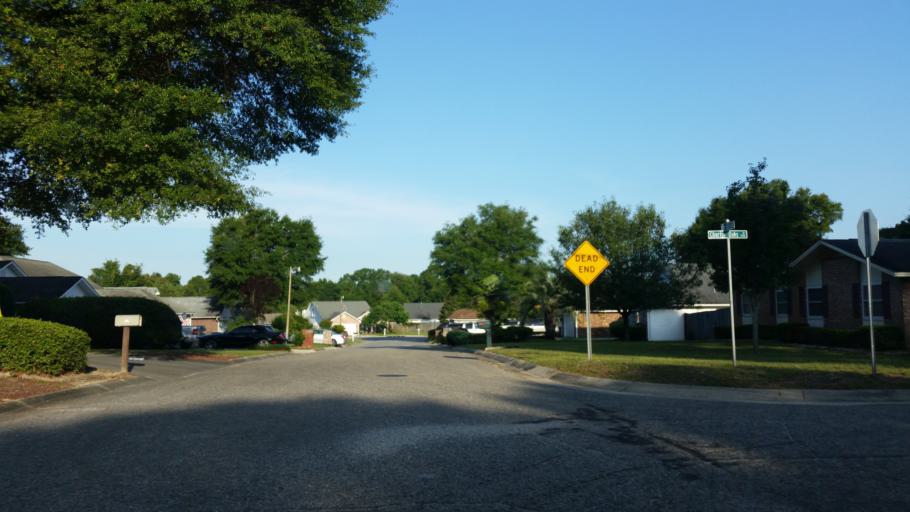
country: US
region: Florida
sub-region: Escambia County
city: Ferry Pass
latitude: 30.5059
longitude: -87.2018
